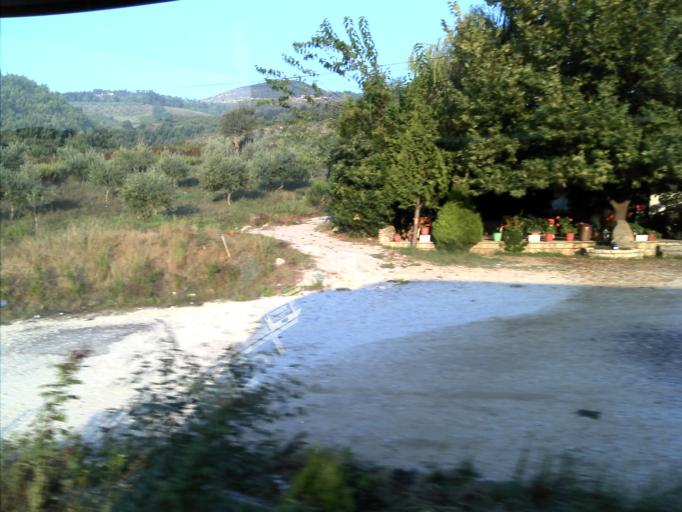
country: AL
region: Gjirokaster
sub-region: Rrethi i Tepelenes
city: Krahes
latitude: 40.4639
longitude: 19.8526
